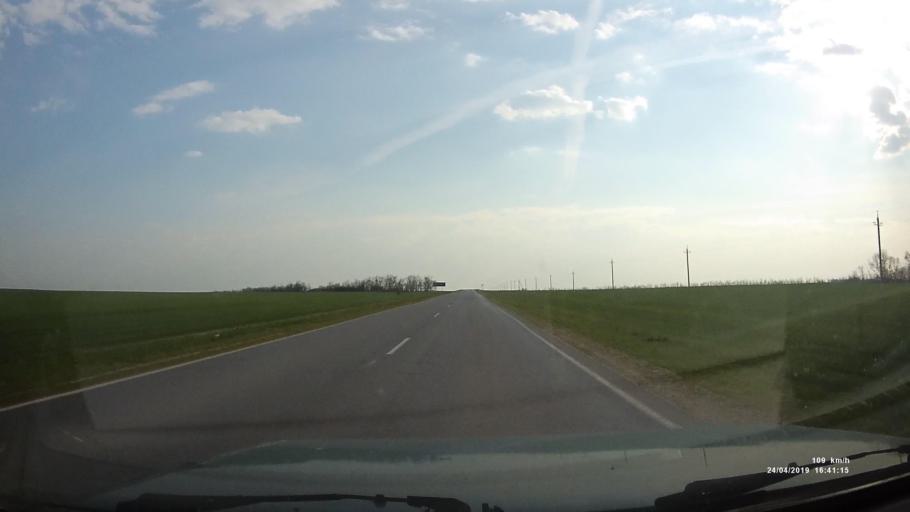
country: RU
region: Rostov
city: Gundorovskiy
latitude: 46.8226
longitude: 41.8700
